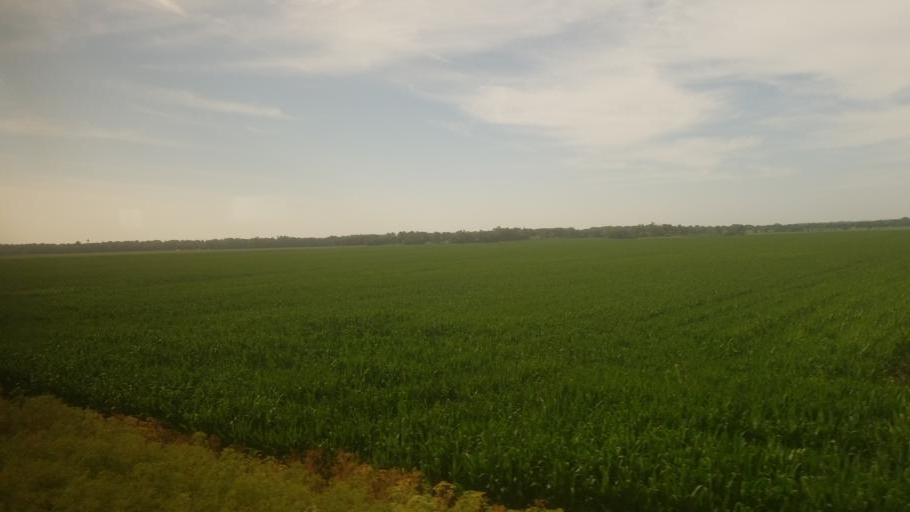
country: US
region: Kansas
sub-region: Douglas County
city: Eudora
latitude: 38.9498
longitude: -95.1397
